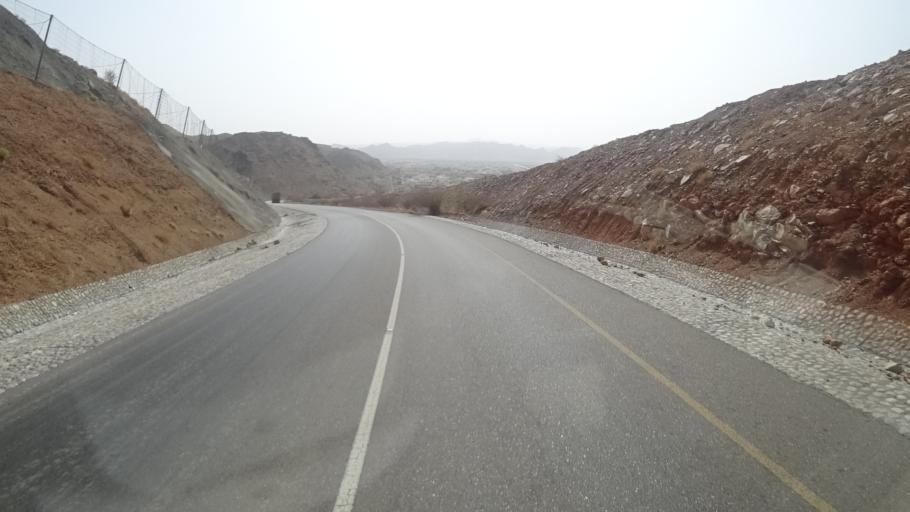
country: OM
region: Muhafazat ad Dakhiliyah
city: Nizwa
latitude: 23.0059
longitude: 57.5691
